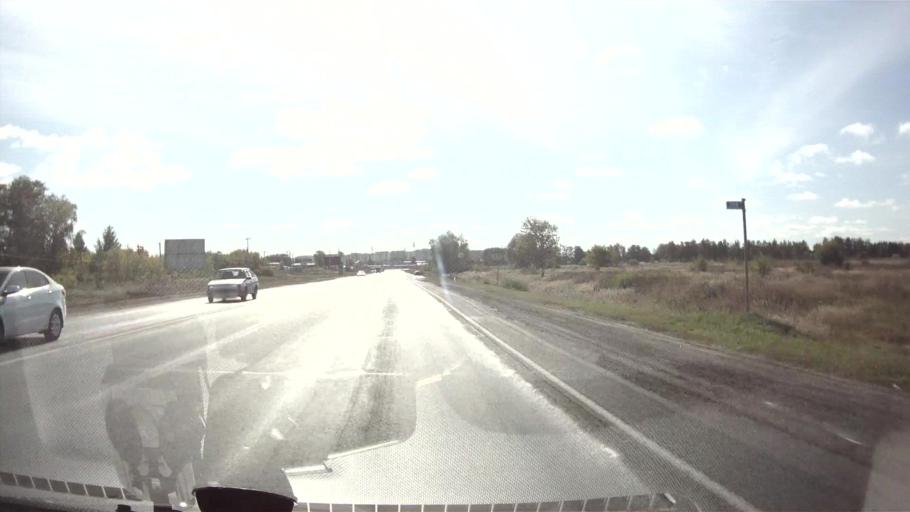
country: RU
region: Ulyanovsk
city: Isheyevka
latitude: 54.2966
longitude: 48.2488
